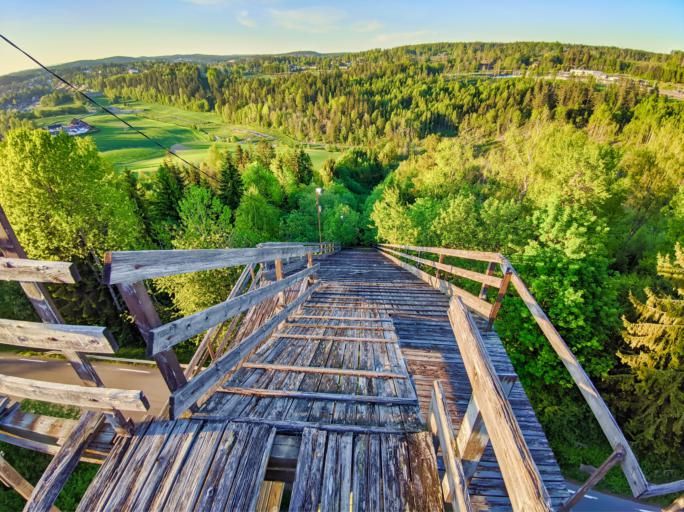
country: NO
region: Akershus
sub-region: Ski
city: Ski
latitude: 59.7377
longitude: 10.8299
